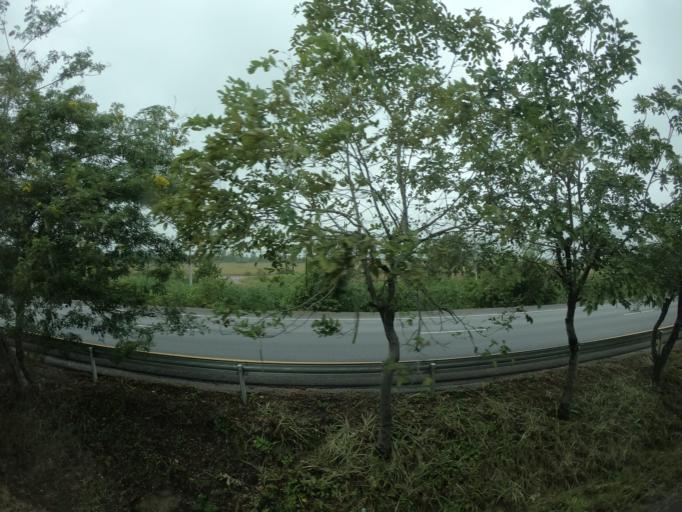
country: TH
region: Nakhon Ratchasima
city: Phimai
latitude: 15.3225
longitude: 102.4350
